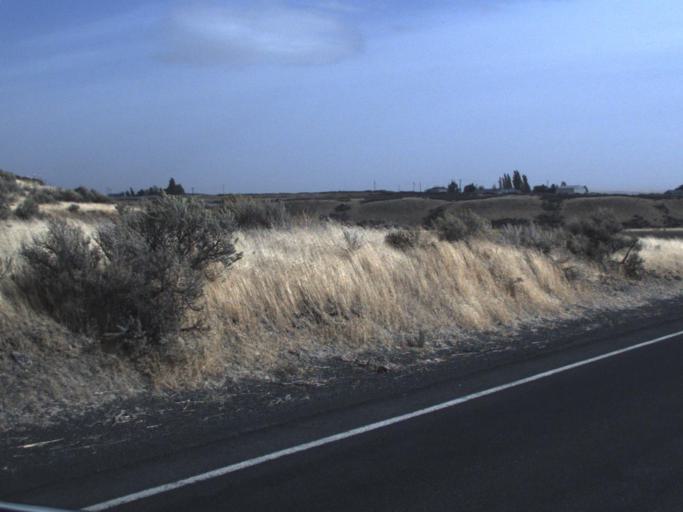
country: US
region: Washington
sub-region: Adams County
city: Ritzville
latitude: 47.3442
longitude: -118.6919
